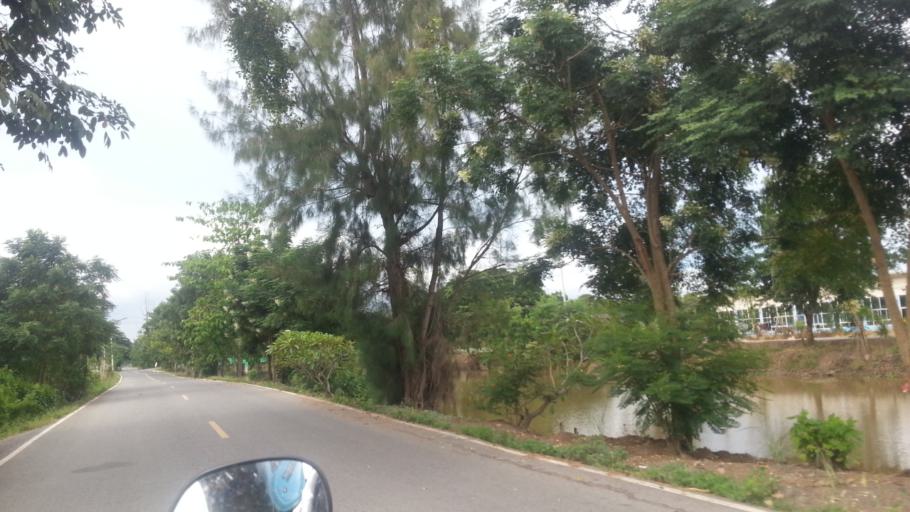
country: TH
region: Pathum Thani
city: Nong Suea
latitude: 14.1901
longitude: 100.8230
